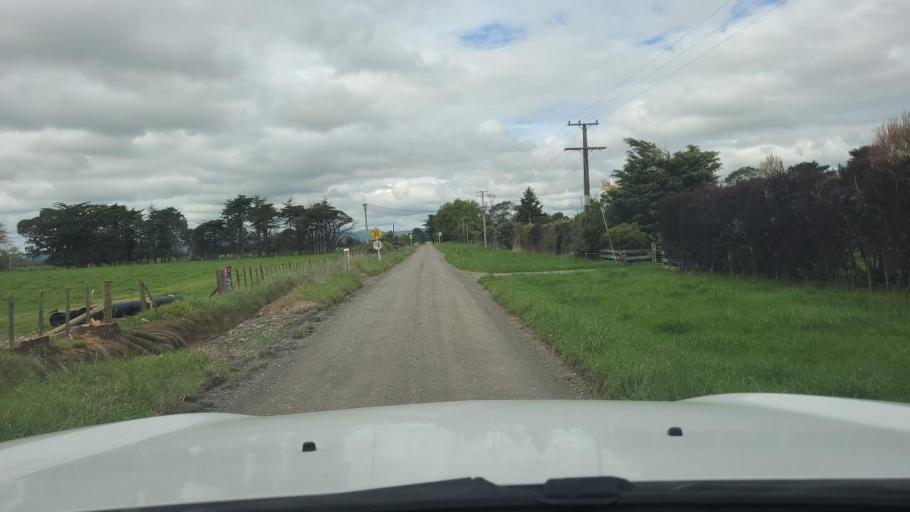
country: NZ
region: Wellington
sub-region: South Wairarapa District
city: Waipawa
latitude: -41.1455
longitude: 175.3797
